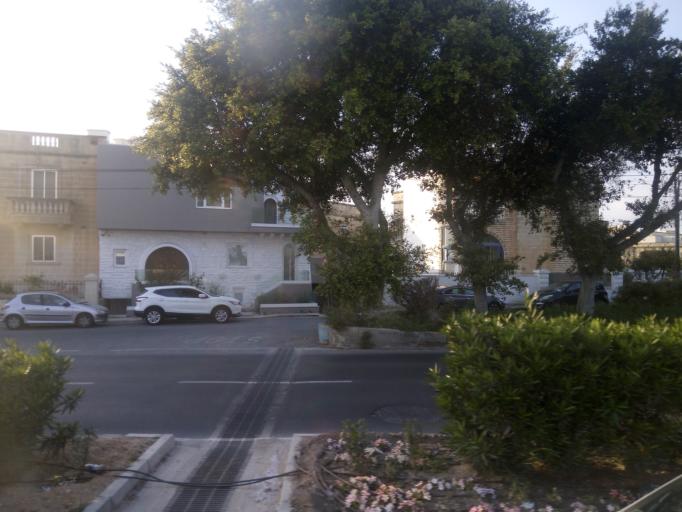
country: MT
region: Attard
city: Attard
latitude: 35.8923
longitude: 14.4491
